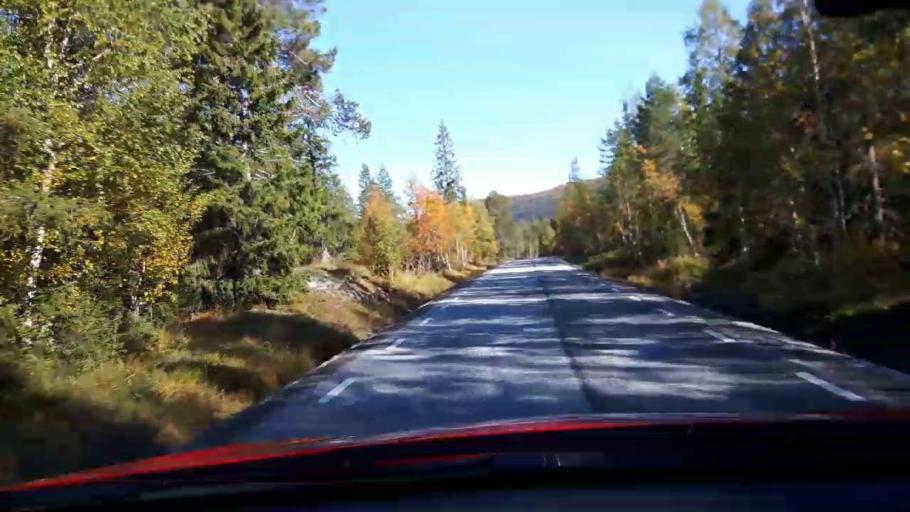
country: NO
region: Nord-Trondelag
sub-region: Royrvik
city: Royrvik
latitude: 64.8190
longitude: 14.2241
